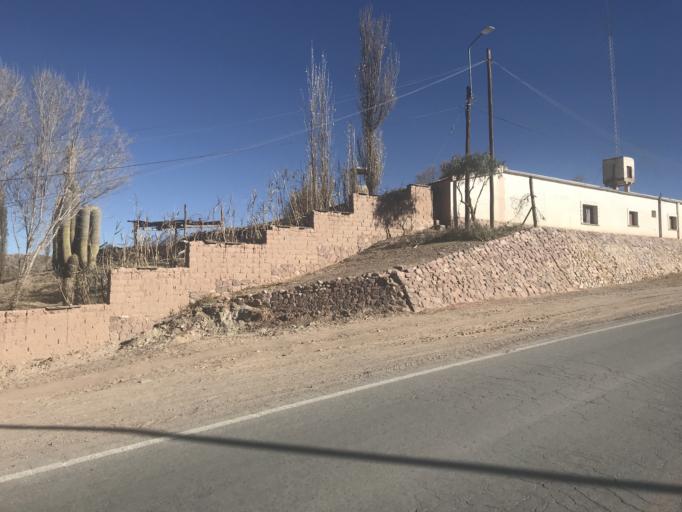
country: AR
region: Jujuy
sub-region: Departamento de Humahuaca
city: Humahuaca
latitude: -23.2144
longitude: -65.3482
